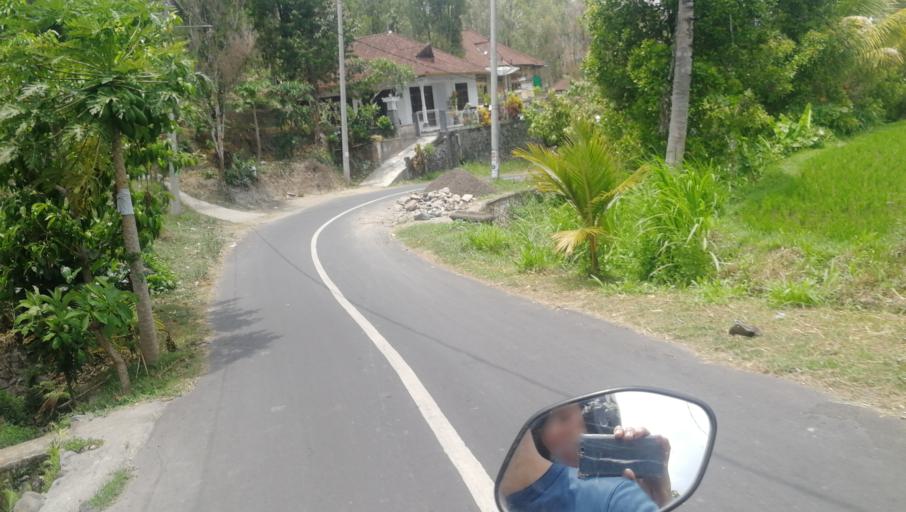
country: ID
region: Bali
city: Banjar Pedawa
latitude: -8.2658
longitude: 115.0285
